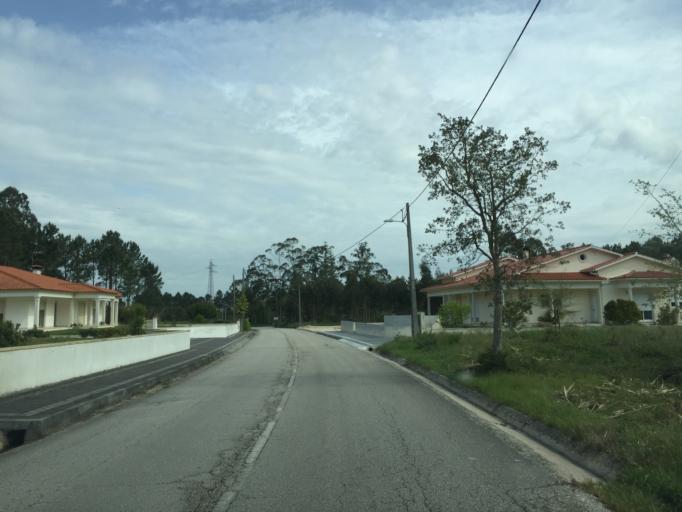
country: PT
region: Coimbra
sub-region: Figueira da Foz
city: Lavos
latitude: 40.0176
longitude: -8.8228
